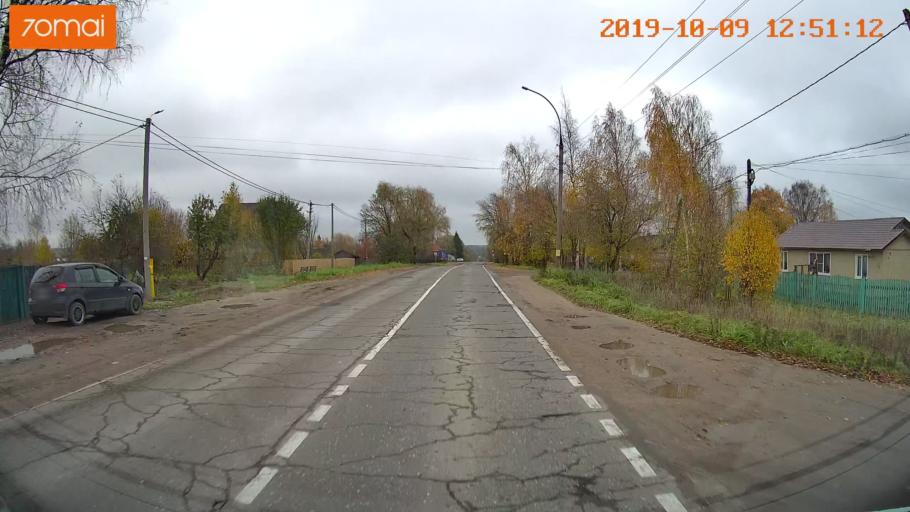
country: RU
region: Jaroslavl
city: Prechistoye
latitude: 58.4208
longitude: 40.3385
